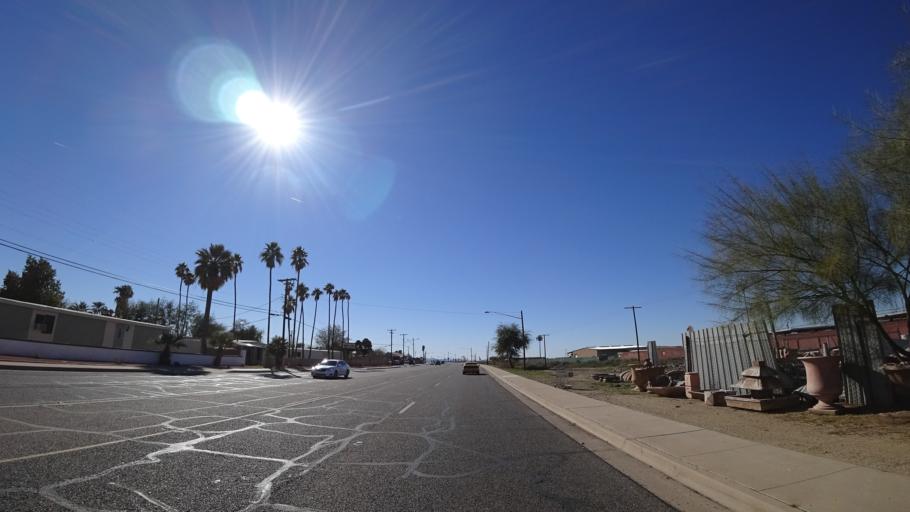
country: US
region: Arizona
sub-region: Maricopa County
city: Goodyear
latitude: 33.4270
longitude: -112.3537
